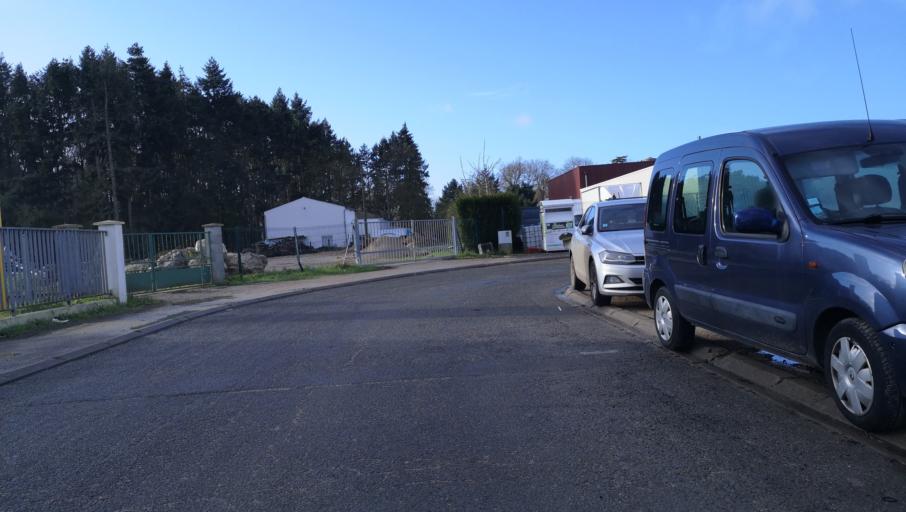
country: FR
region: Centre
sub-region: Departement du Loiret
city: Saint-Pryve-Saint-Mesmin
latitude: 47.8743
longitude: 1.8522
